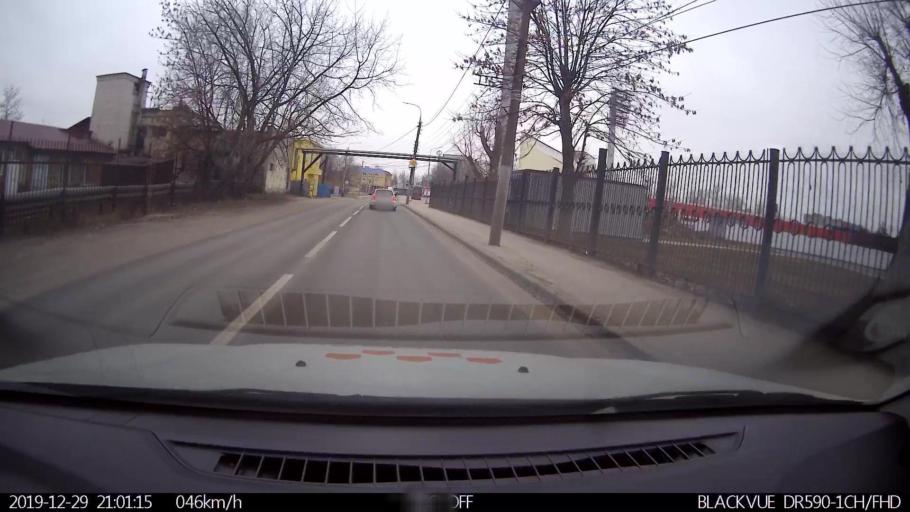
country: RU
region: Nizjnij Novgorod
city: Nizhniy Novgorod
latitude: 56.3081
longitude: 43.9286
